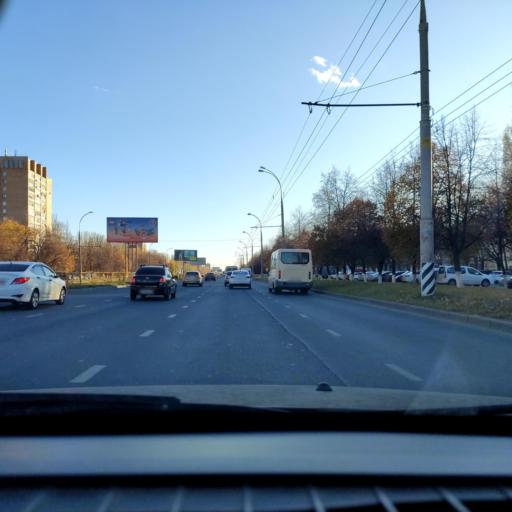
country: RU
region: Samara
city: Tol'yatti
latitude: 53.5252
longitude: 49.2962
